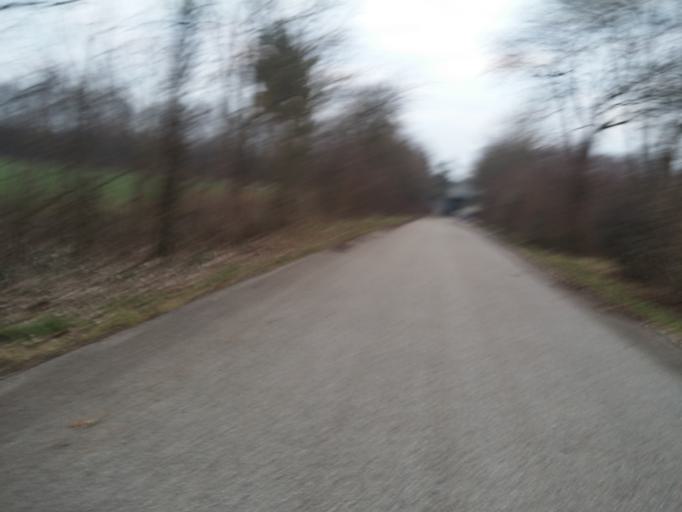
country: DE
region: Bavaria
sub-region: Upper Bavaria
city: Putzbrunn
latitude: 48.0699
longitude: 11.7184
